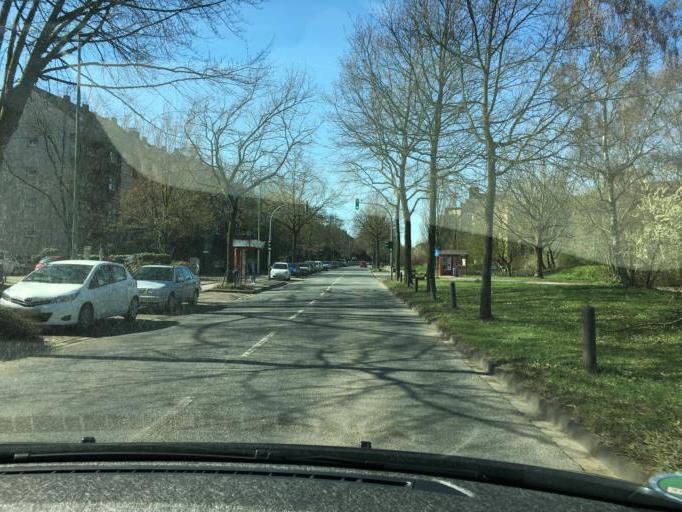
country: DE
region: North Rhine-Westphalia
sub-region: Regierungsbezirk Dusseldorf
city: Duisburg
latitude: 51.4413
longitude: 6.7882
